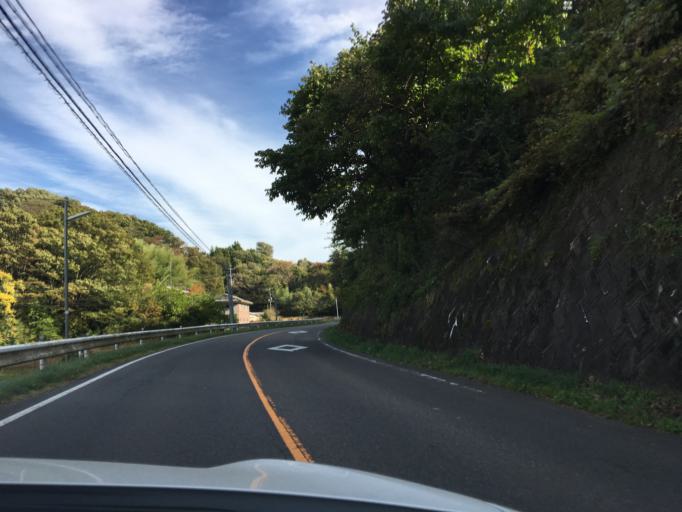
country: JP
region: Fukushima
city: Miharu
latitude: 37.3603
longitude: 140.4701
